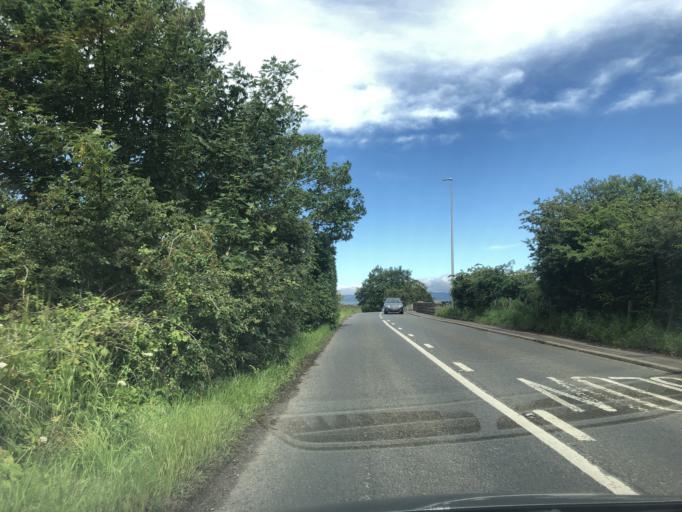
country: GB
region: Scotland
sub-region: Angus
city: Forfar
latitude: 56.6532
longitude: -2.8916
